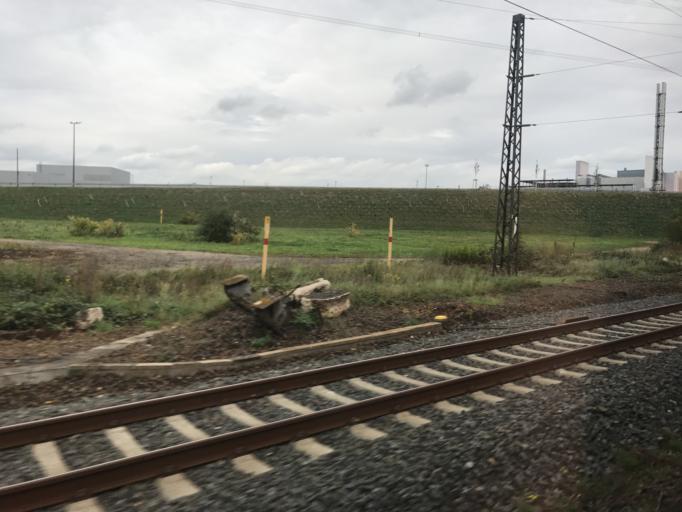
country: DE
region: Hesse
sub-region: Regierungsbezirk Darmstadt
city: Bischofsheim
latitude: 49.9842
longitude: 8.3839
